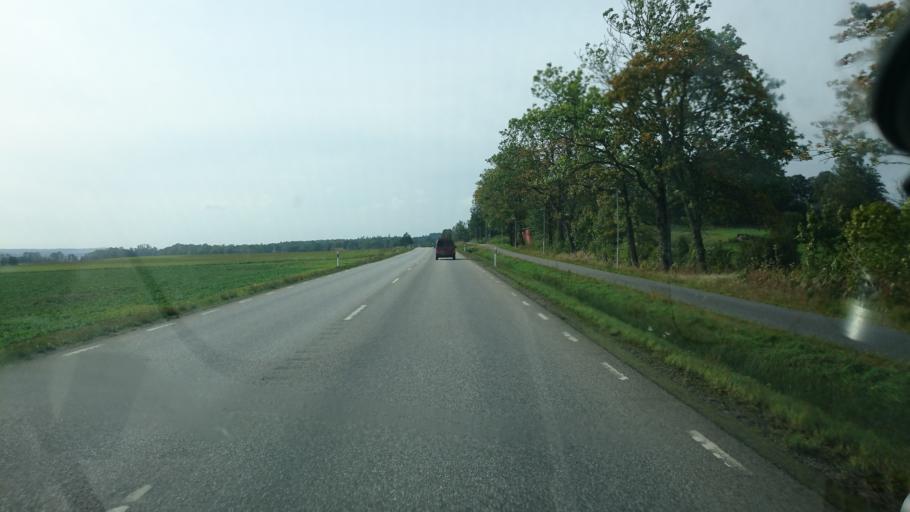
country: SE
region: Vaestra Goetaland
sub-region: Alingsas Kommun
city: Sollebrunn
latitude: 58.0940
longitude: 12.5016
